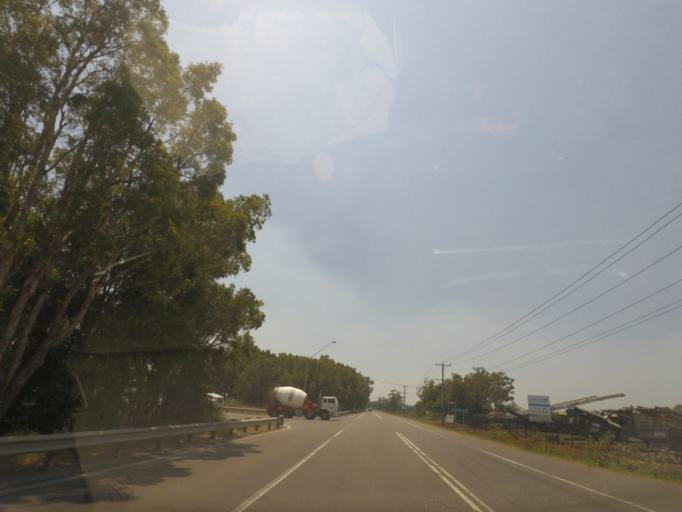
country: AU
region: New South Wales
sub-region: Newcastle
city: Mayfield West
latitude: -32.8323
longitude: 151.7253
